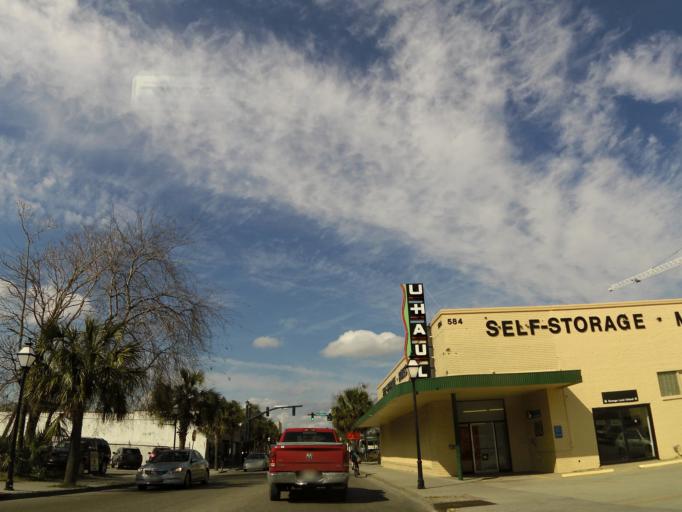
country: US
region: South Carolina
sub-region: Charleston County
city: Charleston
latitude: 32.7933
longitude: -79.9415
